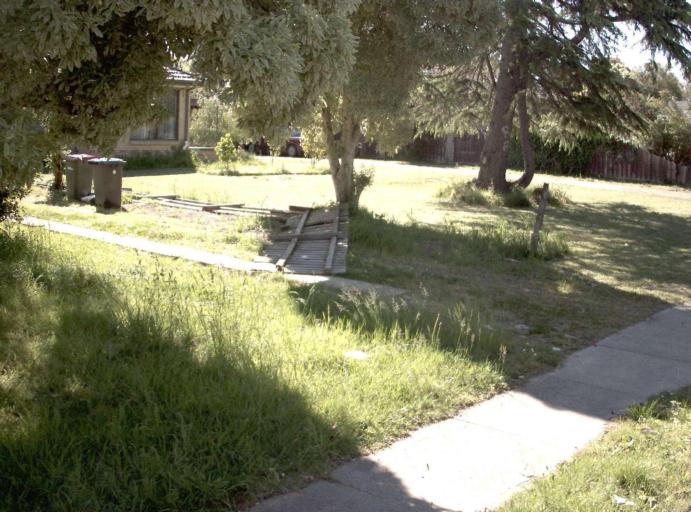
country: AU
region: Victoria
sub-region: Knox
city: Knoxfield
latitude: -37.8881
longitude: 145.2576
